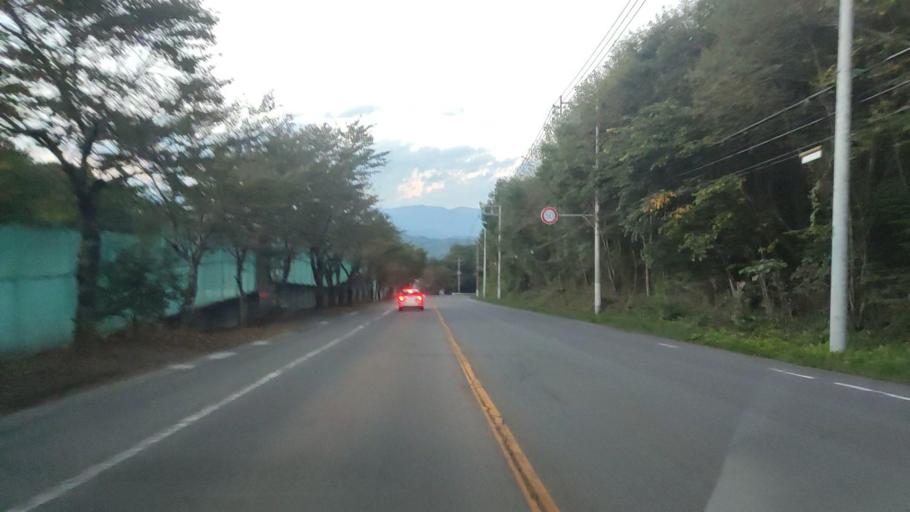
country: JP
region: Gunma
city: Nakanojomachi
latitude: 36.5360
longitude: 138.6091
